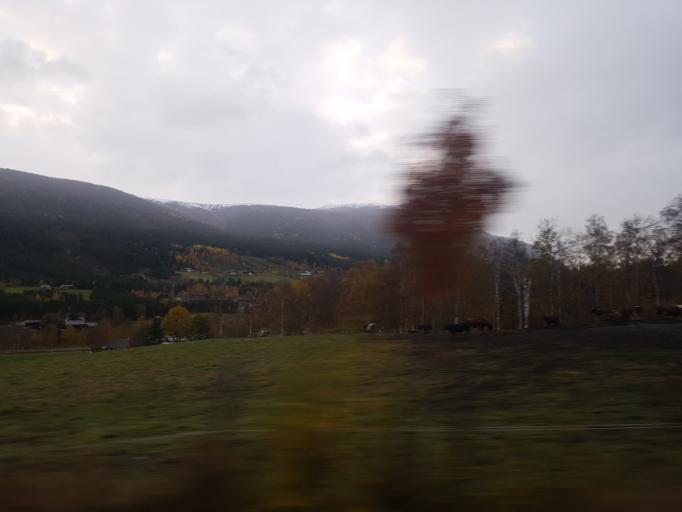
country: NO
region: Oppland
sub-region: Dovre
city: Dovre
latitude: 61.9931
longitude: 9.2362
